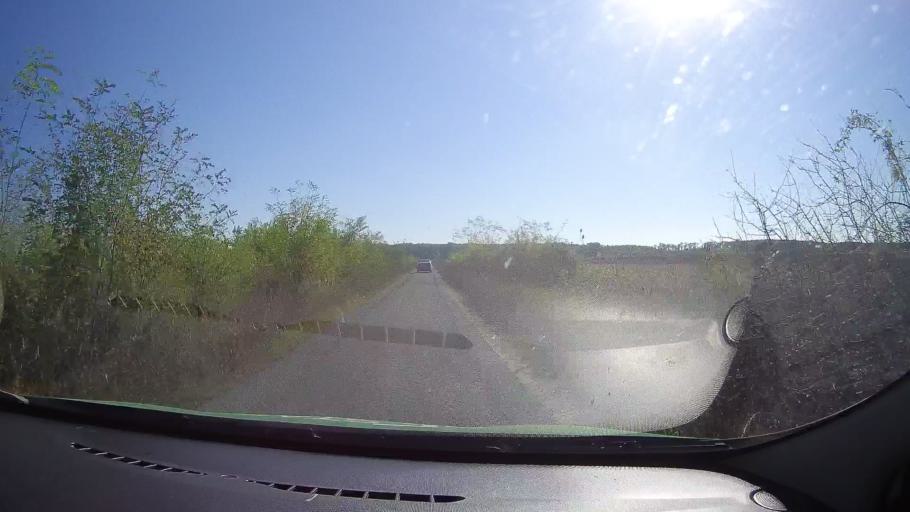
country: RO
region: Satu Mare
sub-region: Comuna Doba
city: Doba
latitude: 47.7225
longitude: 22.7250
